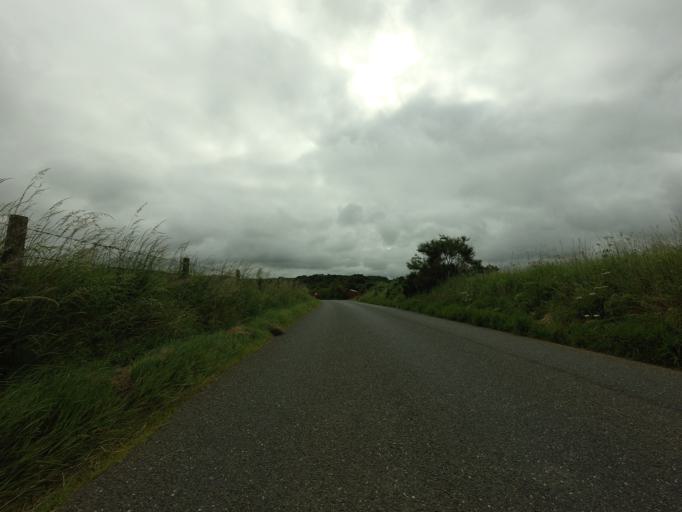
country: GB
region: Scotland
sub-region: Aberdeenshire
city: Turriff
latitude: 57.5337
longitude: -2.4220
